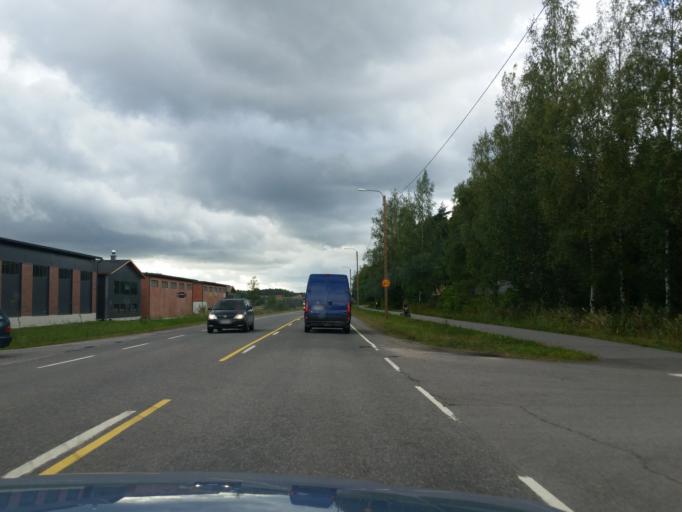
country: FI
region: Varsinais-Suomi
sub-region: Turku
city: Kaarina
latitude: 60.4105
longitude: 22.4038
